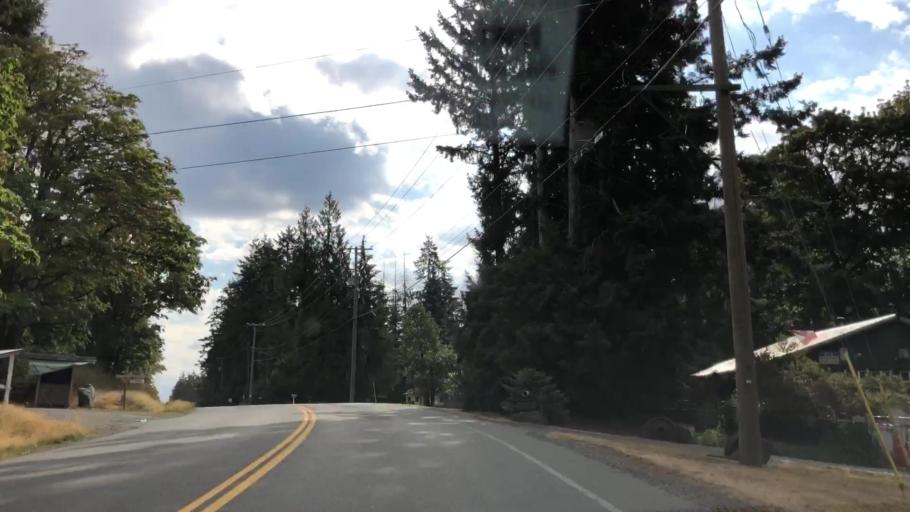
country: CA
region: British Columbia
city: North Saanich
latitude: 48.6865
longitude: -123.5630
